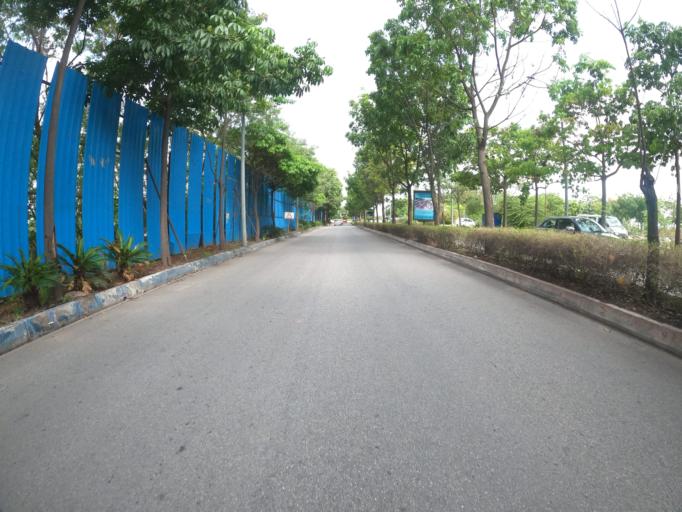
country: IN
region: Telangana
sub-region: Rangareddi
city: Kukatpalli
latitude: 17.4102
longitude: 78.3715
